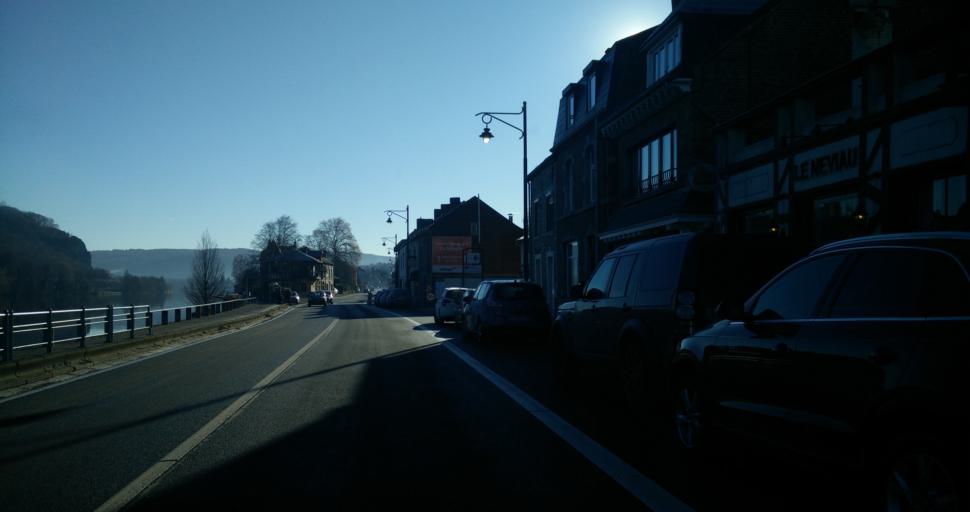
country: BE
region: Wallonia
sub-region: Province de Namur
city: Namur
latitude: 50.4328
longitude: 4.8633
